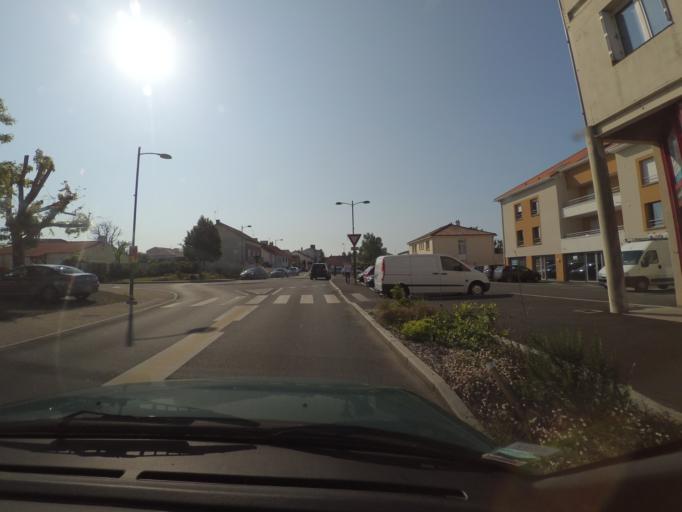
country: FR
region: Pays de la Loire
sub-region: Departement de la Loire-Atlantique
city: Le Pallet
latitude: 47.1406
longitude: -1.3391
